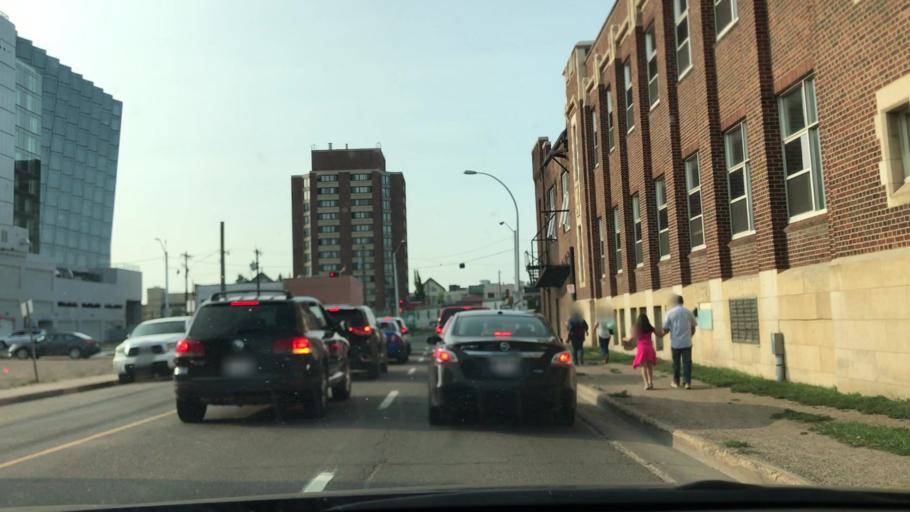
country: CA
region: Alberta
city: Edmonton
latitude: 53.5434
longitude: -113.4805
